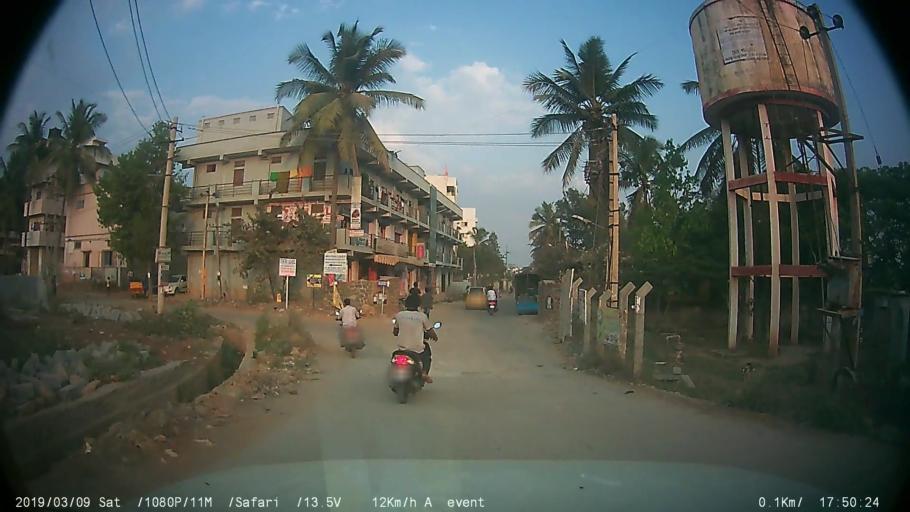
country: IN
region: Karnataka
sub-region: Bangalore Urban
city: Anekal
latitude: 12.8281
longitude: 77.6859
